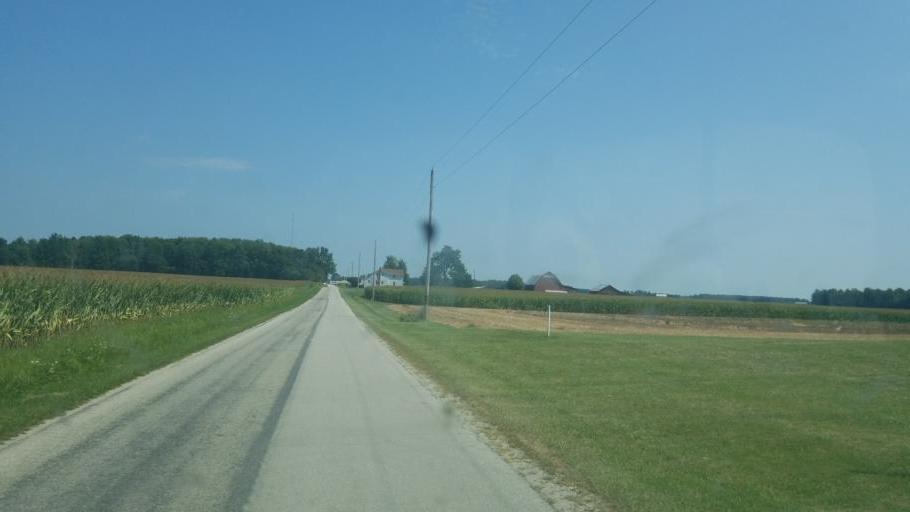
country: US
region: Ohio
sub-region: Crawford County
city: Bucyrus
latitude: 40.9357
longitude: -82.9648
